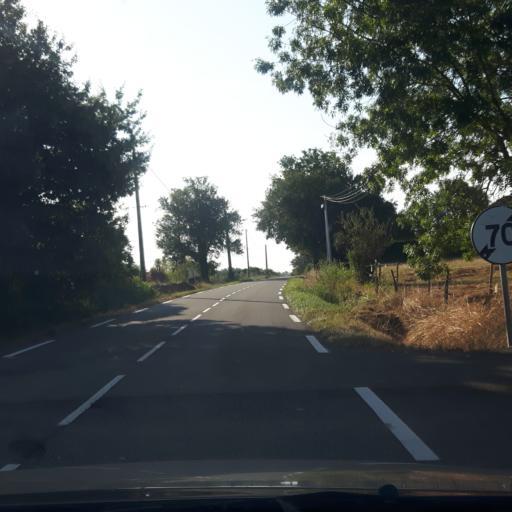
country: FR
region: Midi-Pyrenees
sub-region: Departement de la Haute-Garonne
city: Vacquiers
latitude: 43.7581
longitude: 1.5040
